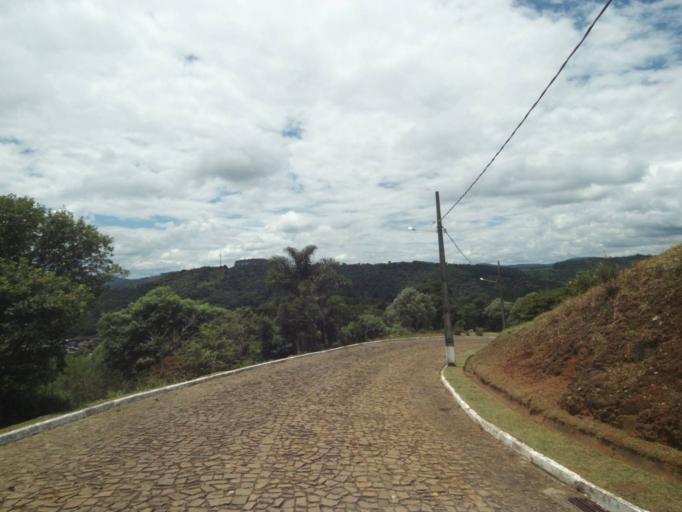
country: BR
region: Parana
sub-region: Pinhao
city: Pinhao
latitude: -26.1614
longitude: -51.5592
